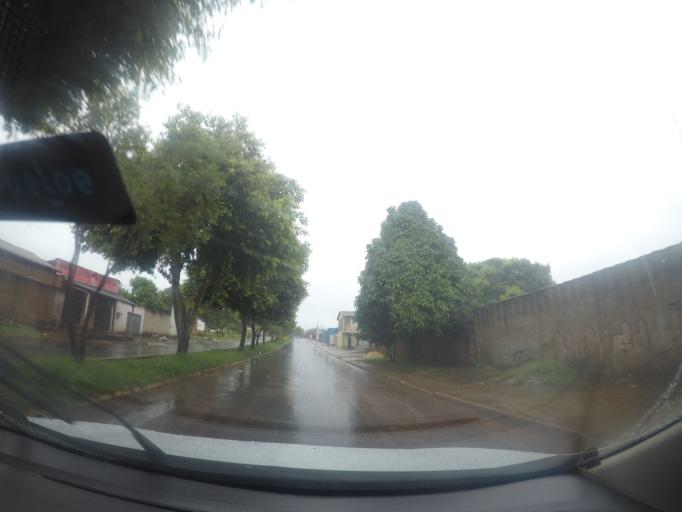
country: BR
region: Goias
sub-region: Goiania
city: Goiania
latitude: -16.6048
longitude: -49.3438
